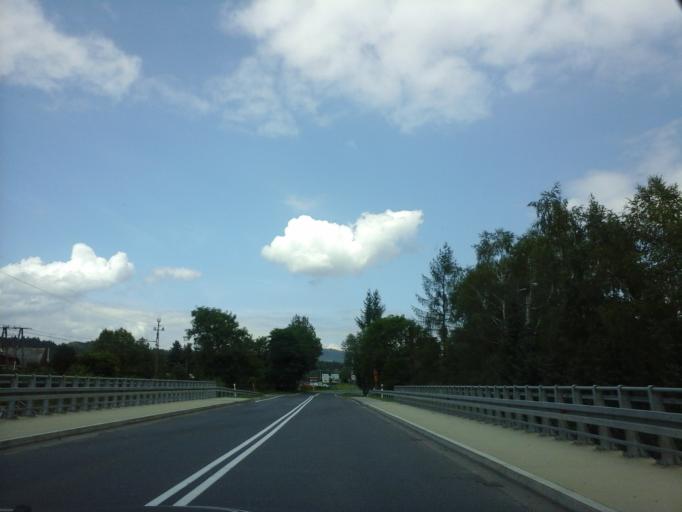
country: PL
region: Lesser Poland Voivodeship
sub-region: Powiat suski
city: Juszczyn
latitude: 49.7086
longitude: 19.6903
